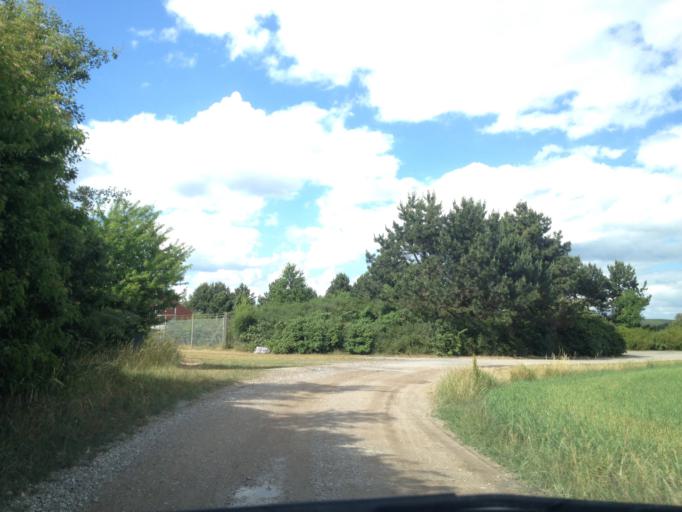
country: DK
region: Central Jutland
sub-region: Syddjurs Kommune
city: Ronde
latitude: 56.2047
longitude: 10.4834
